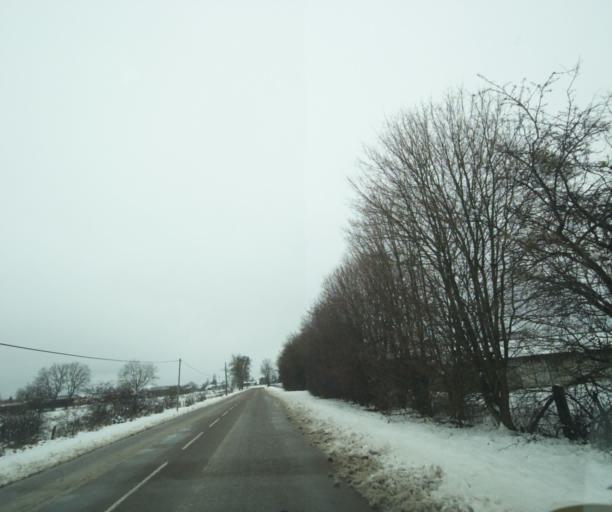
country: FR
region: Champagne-Ardenne
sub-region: Departement de la Haute-Marne
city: Montier-en-Der
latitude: 48.4533
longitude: 4.7741
